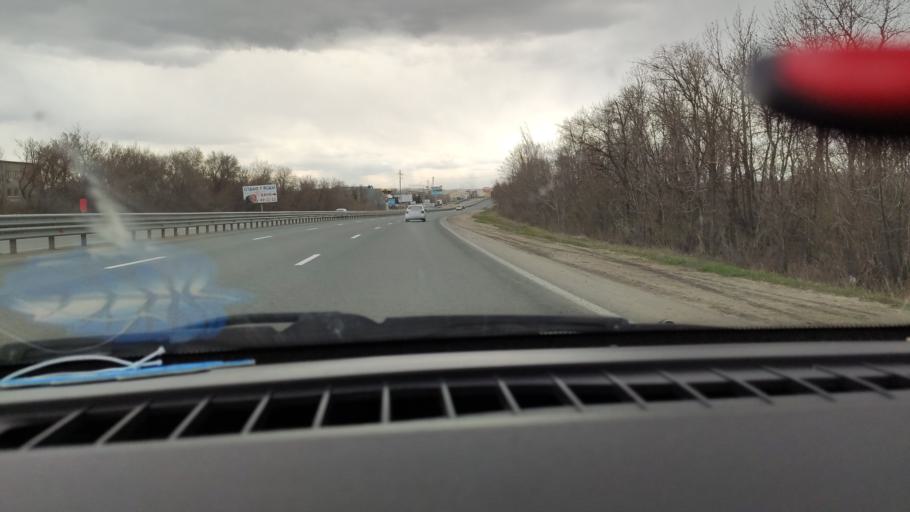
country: RU
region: Saratov
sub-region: Saratovskiy Rayon
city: Saratov
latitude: 51.6498
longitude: 45.9937
